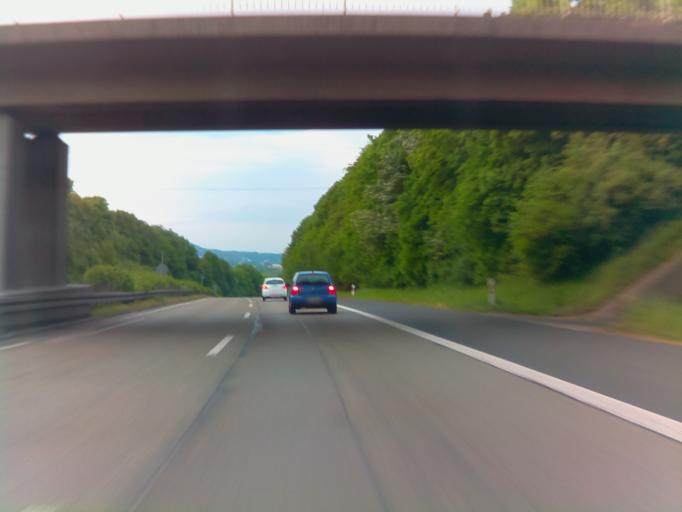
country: DE
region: Hesse
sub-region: Regierungsbezirk Kassel
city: Baunatal
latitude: 51.2311
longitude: 9.4263
